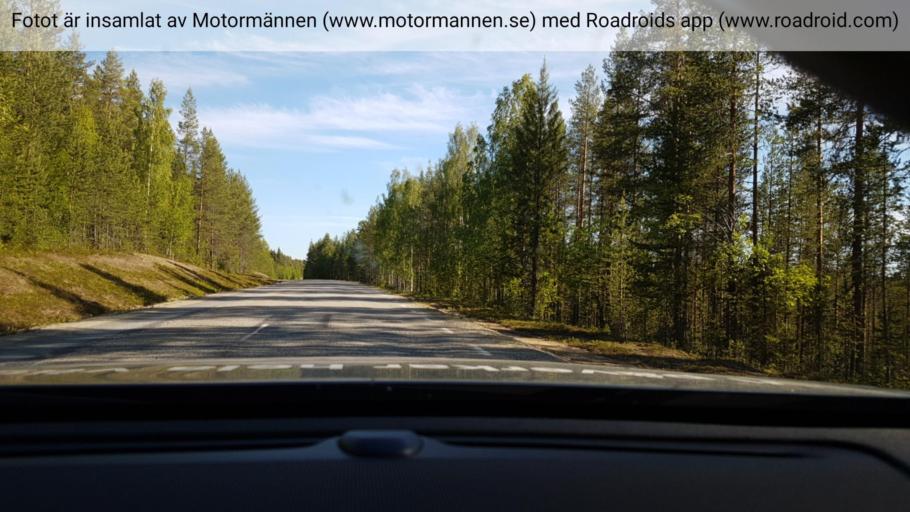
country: SE
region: Vaesterbotten
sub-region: Norsjo Kommun
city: Norsjoe
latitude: 64.6143
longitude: 19.2905
